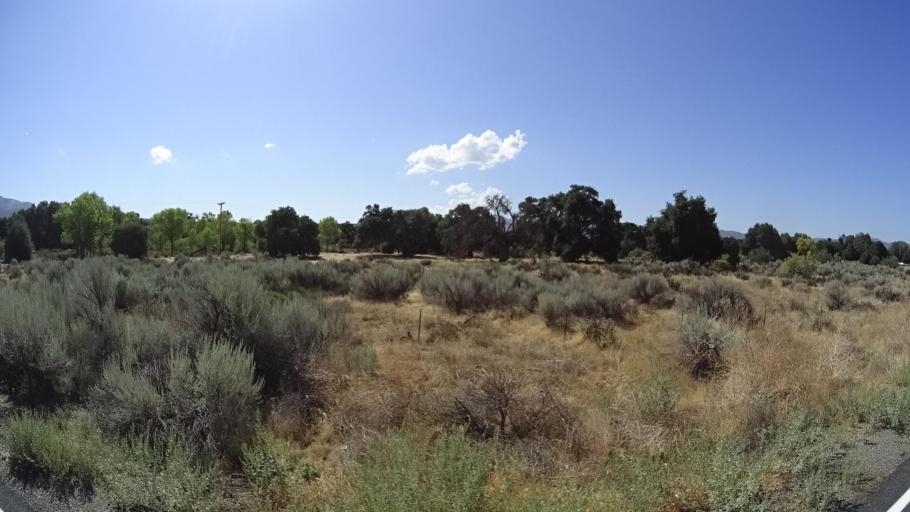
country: US
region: California
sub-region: San Diego County
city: Julian
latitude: 33.2861
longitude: -116.6609
